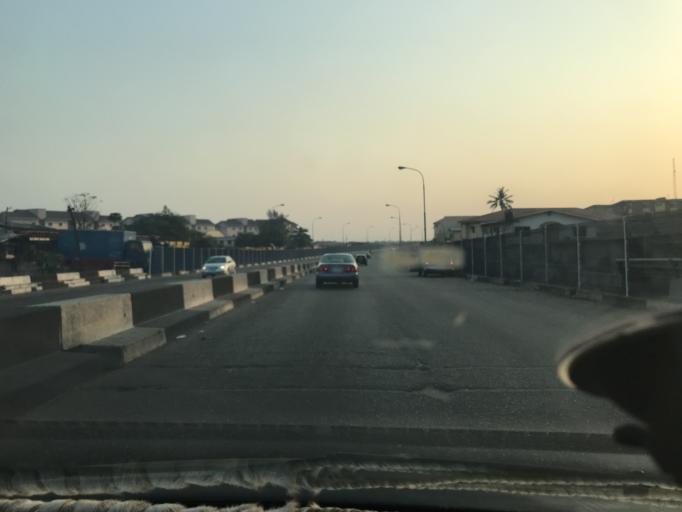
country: NG
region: Lagos
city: Makoko
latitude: 6.4916
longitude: 3.3828
